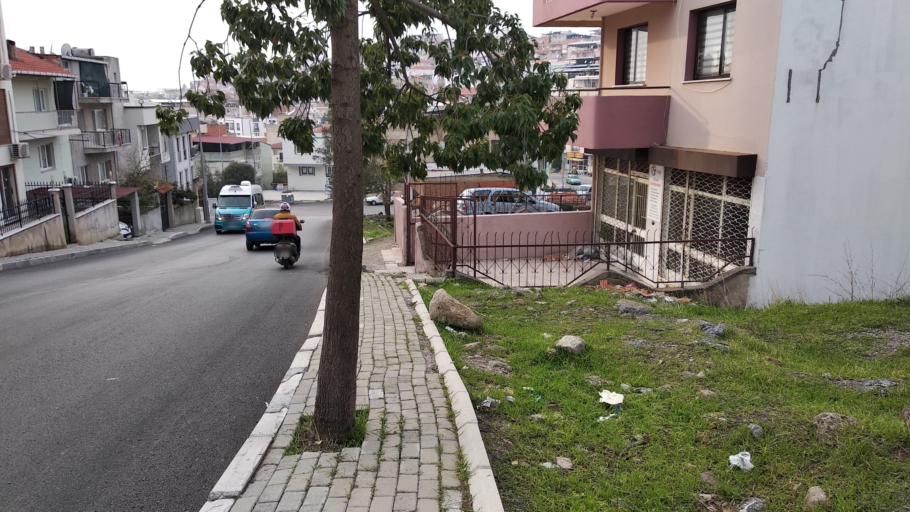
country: TR
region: Izmir
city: Karsiyaka
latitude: 38.4944
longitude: 27.0765
